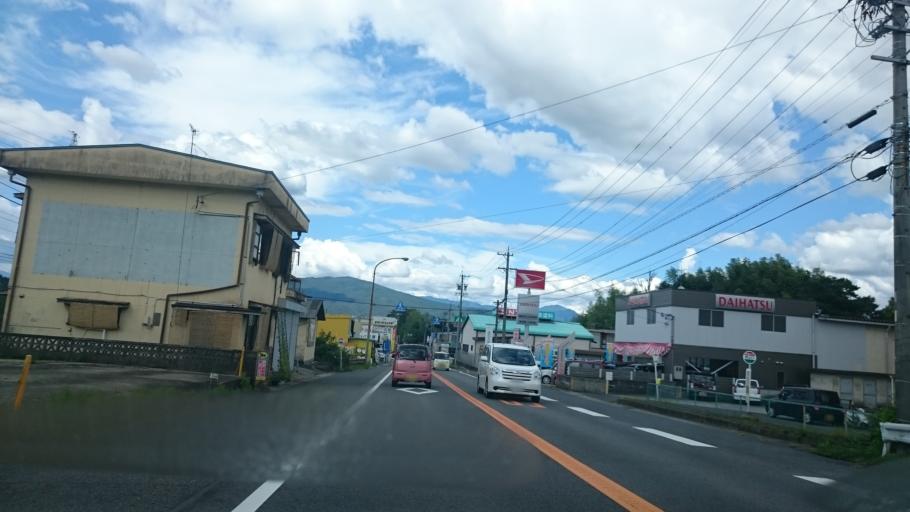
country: JP
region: Gifu
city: Nakatsugawa
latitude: 35.4825
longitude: 137.4860
